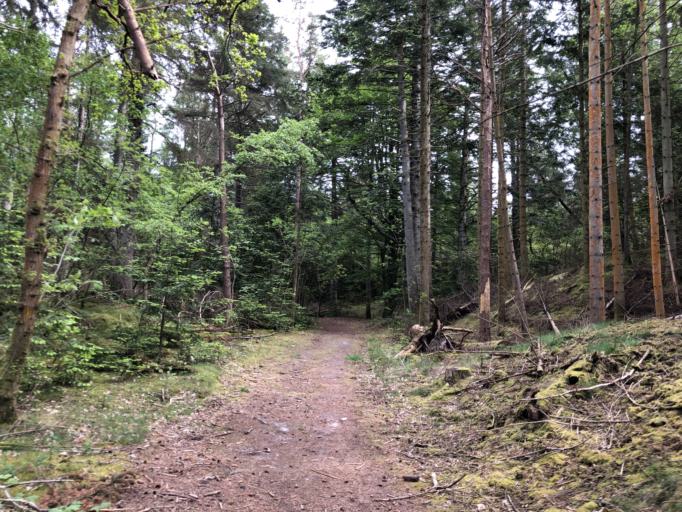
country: DK
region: Central Jutland
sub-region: Holstebro Kommune
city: Ulfborg
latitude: 56.2856
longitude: 8.1769
